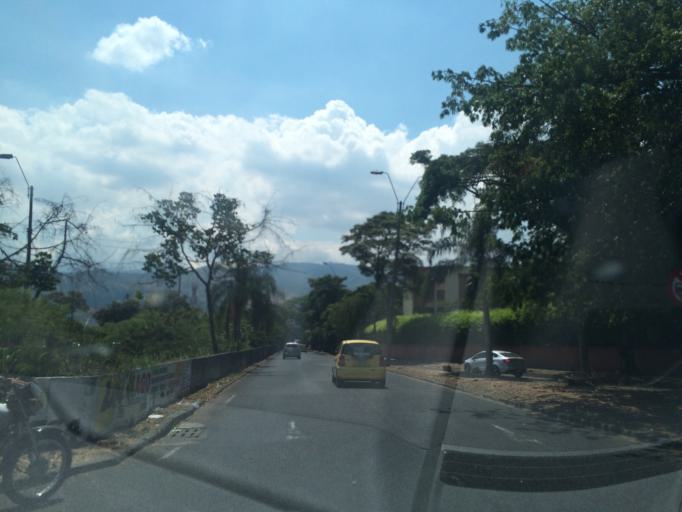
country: CO
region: Valle del Cauca
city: Cali
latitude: 3.4815
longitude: -76.5096
